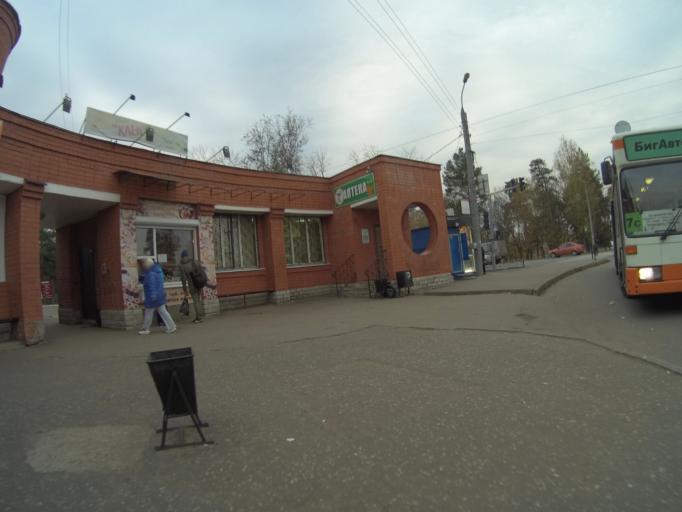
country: RU
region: Vladimir
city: Kommunar
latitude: 56.1031
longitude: 40.4384
